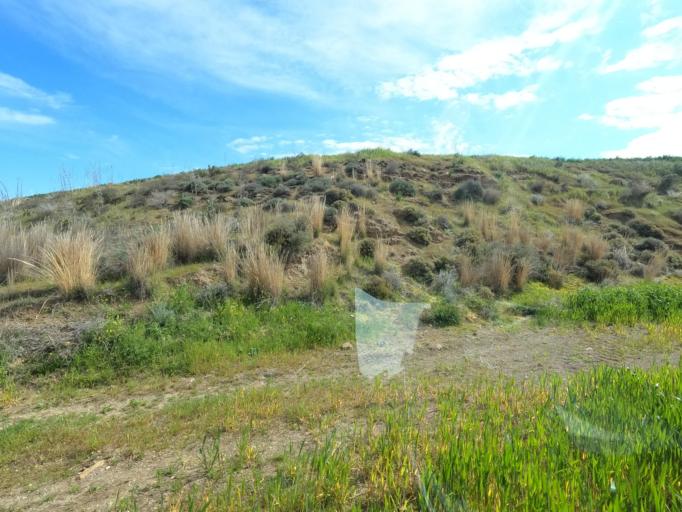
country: CY
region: Lefkosia
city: Lefka
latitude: 35.0982
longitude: 32.9411
